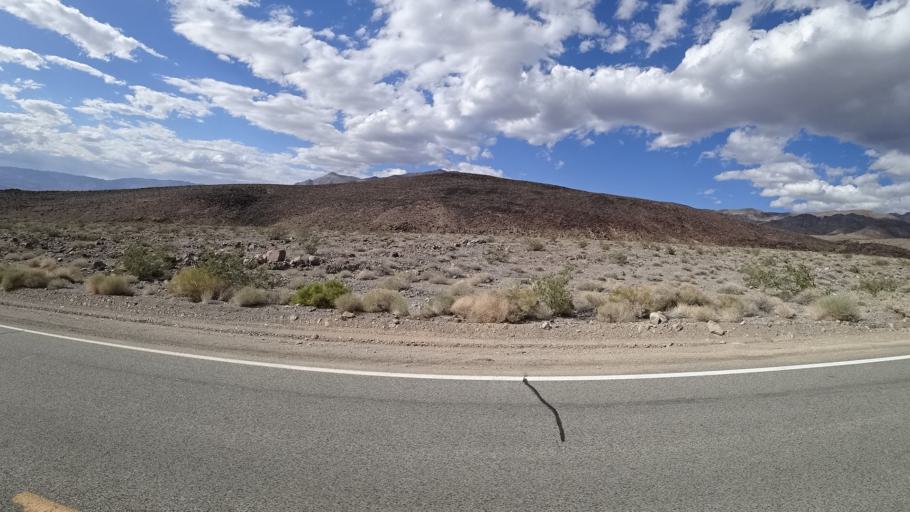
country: US
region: California
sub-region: San Bernardino County
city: Searles Valley
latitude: 36.3483
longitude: -117.3308
